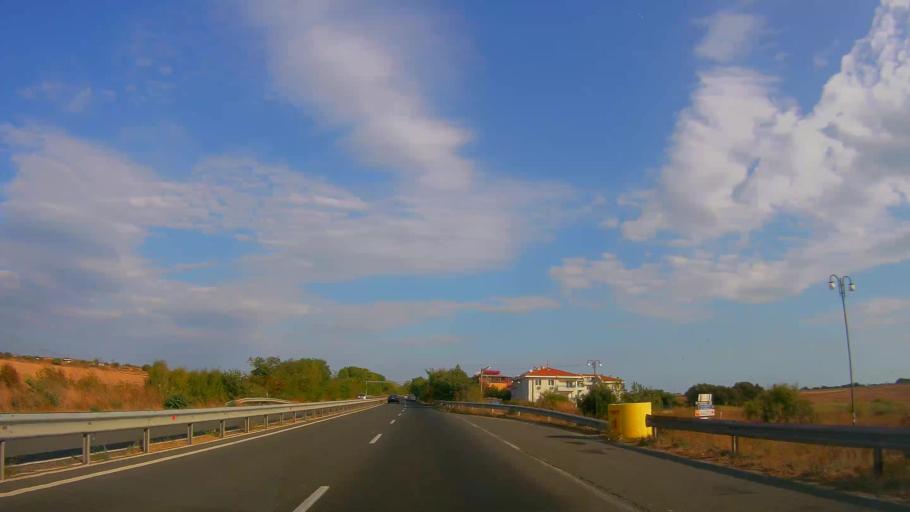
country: BG
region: Burgas
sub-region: Obshtina Sozopol
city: Chernomorets
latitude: 42.4304
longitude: 27.6394
